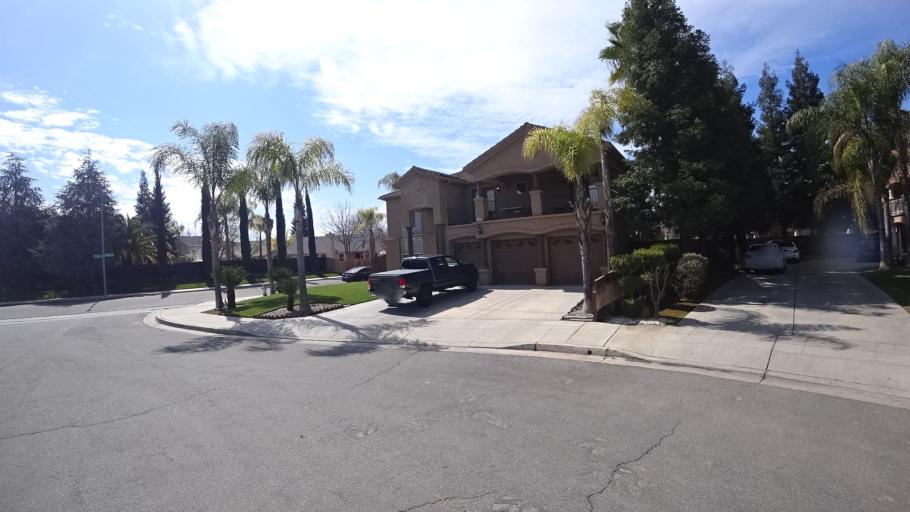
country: US
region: California
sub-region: Fresno County
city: Biola
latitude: 36.8506
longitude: -119.8967
